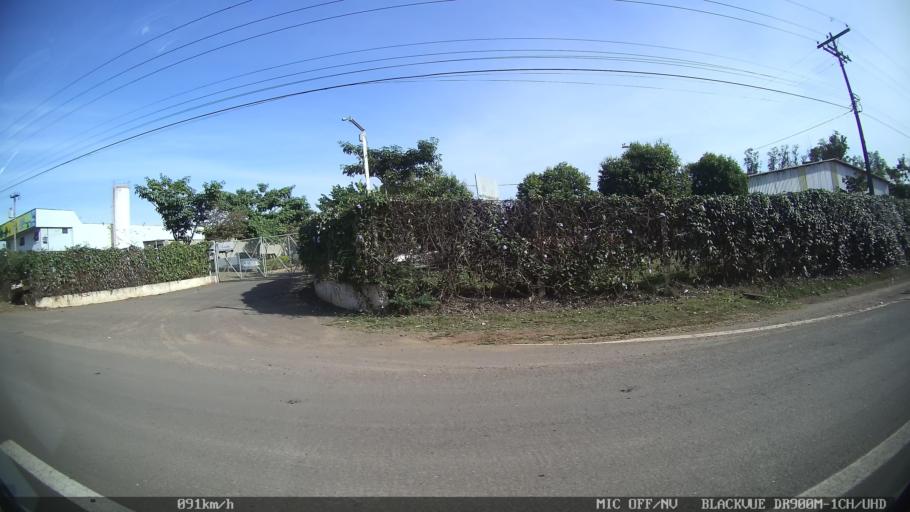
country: BR
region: Sao Paulo
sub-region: Piracicaba
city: Piracicaba
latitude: -22.7735
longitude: -47.6492
